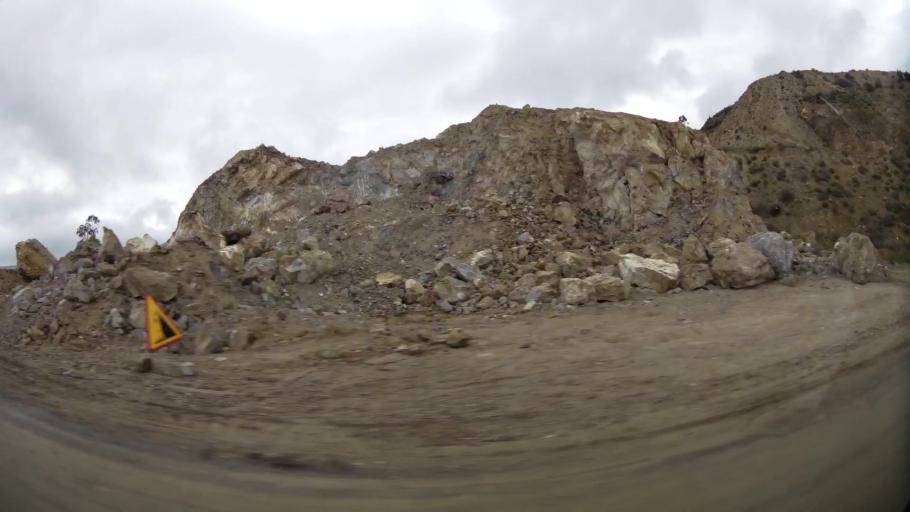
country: MA
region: Taza-Al Hoceima-Taounate
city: Imzourene
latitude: 34.9331
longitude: -3.8128
